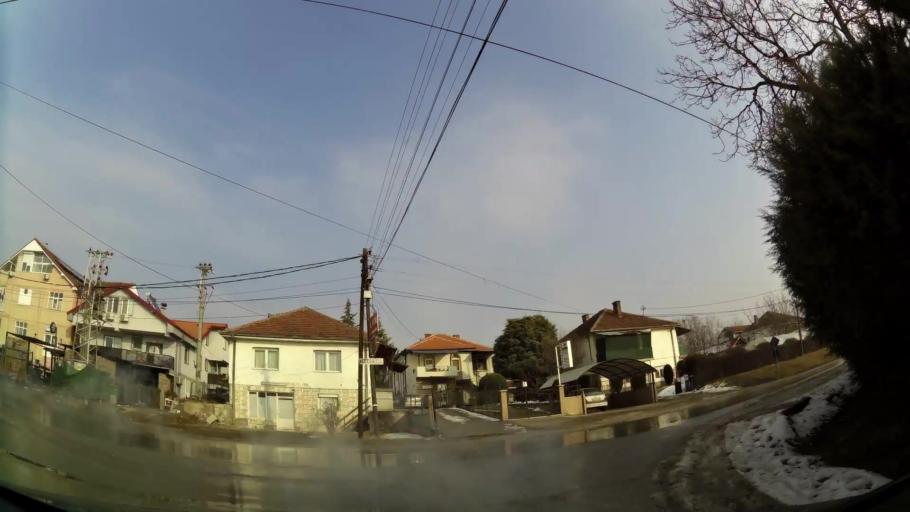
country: MK
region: Ilinden
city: Marino
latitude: 41.9906
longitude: 21.5905
